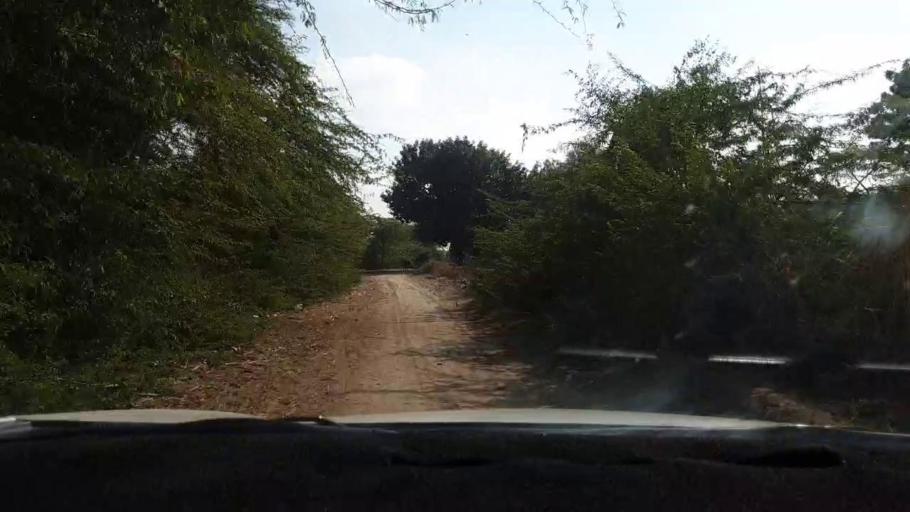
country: PK
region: Sindh
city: Berani
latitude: 25.7604
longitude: 68.9915
